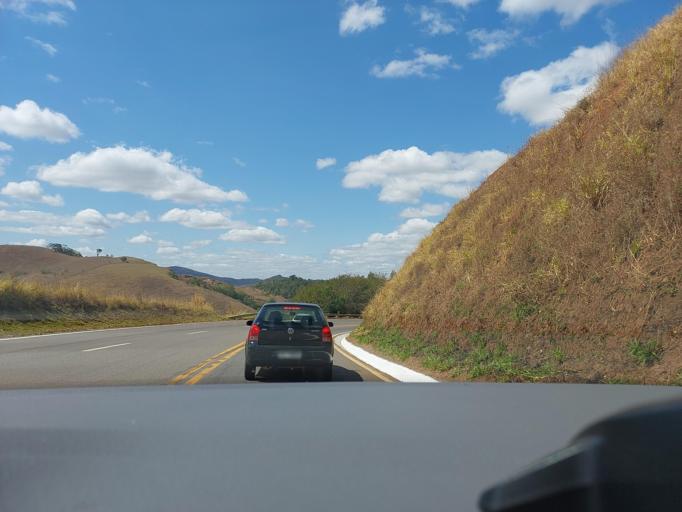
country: BR
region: Minas Gerais
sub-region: Muriae
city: Muriae
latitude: -21.0933
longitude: -42.4740
